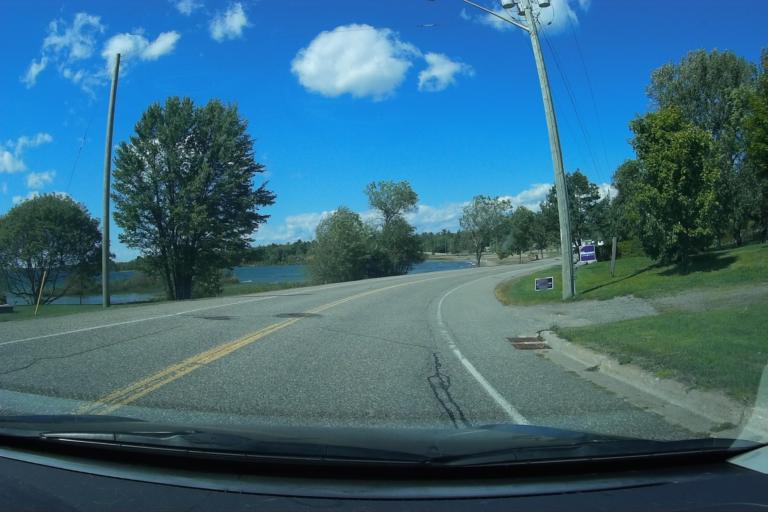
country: CA
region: Ontario
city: Thessalon
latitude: 46.2574
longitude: -83.5645
